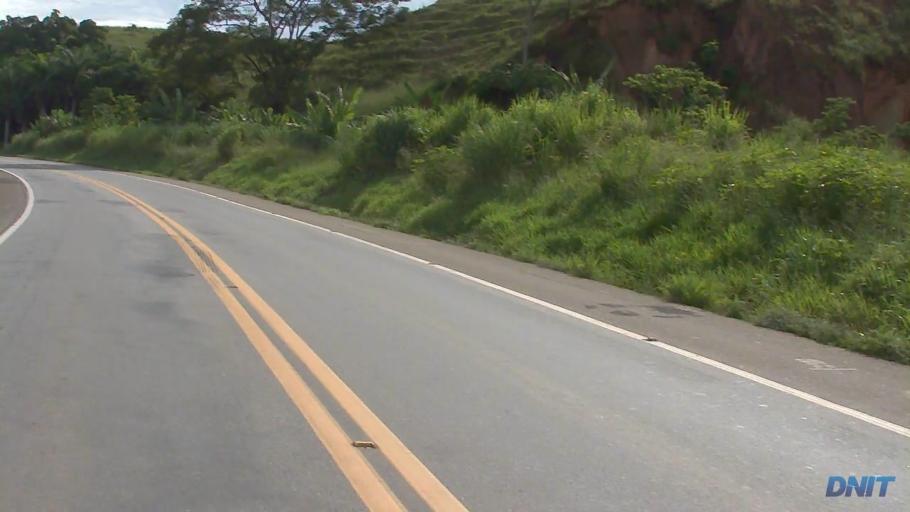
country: BR
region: Minas Gerais
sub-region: Belo Oriente
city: Belo Oriente
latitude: -19.1757
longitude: -42.2551
